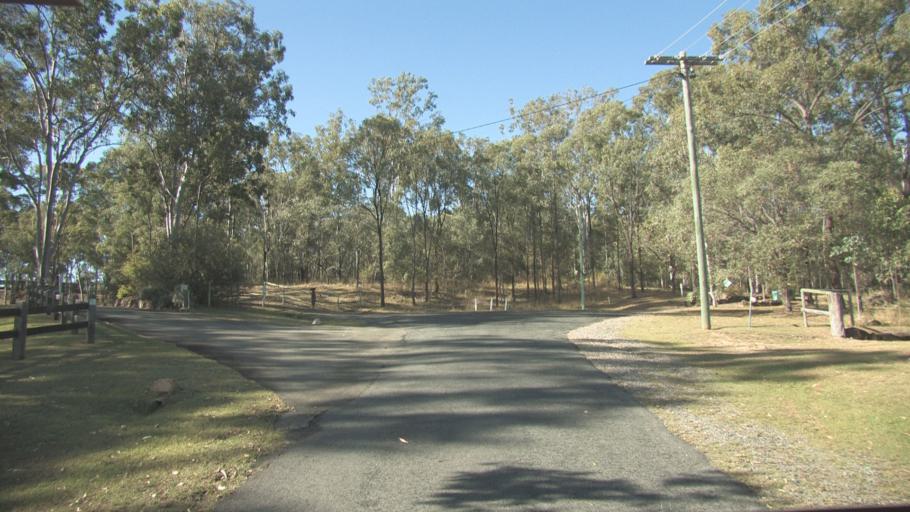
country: AU
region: Queensland
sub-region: Logan
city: Cedar Vale
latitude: -27.8351
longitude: 153.0735
